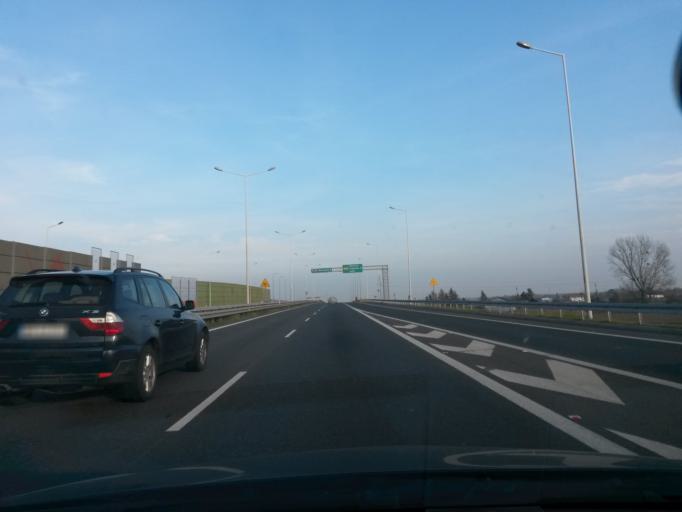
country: PL
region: Lower Silesian Voivodeship
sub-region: Powiat olesnicki
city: Olesnica
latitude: 51.2283
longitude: 17.3650
